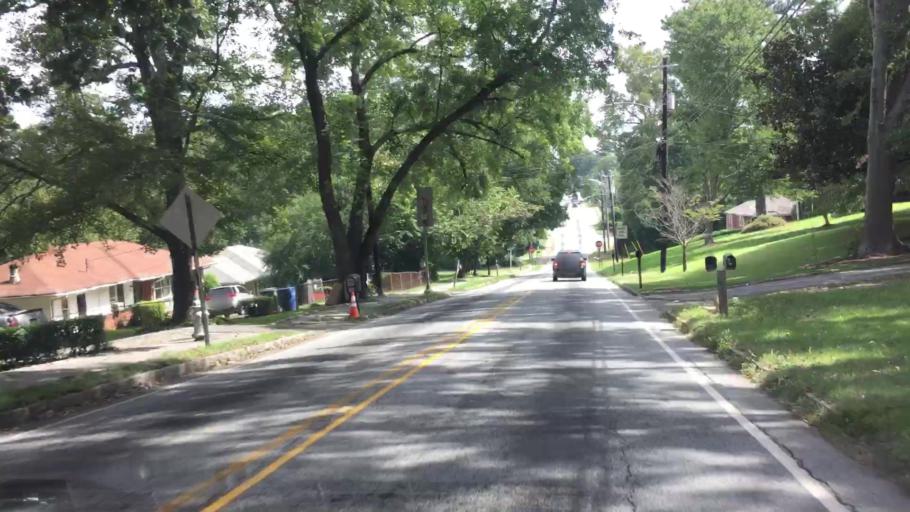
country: US
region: Georgia
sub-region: DeKalb County
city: Gresham Park
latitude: 33.7238
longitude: -84.3269
